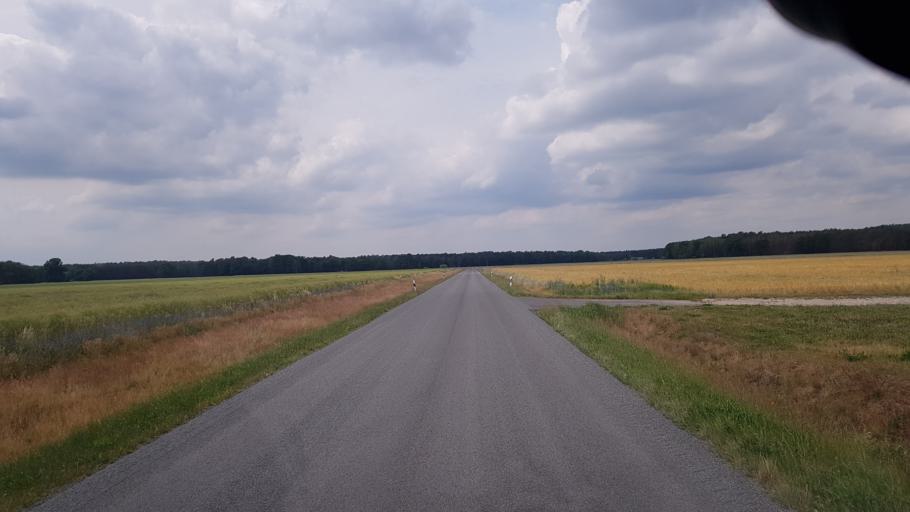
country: DE
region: Brandenburg
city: Ihlow
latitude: 51.8680
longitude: 13.3281
